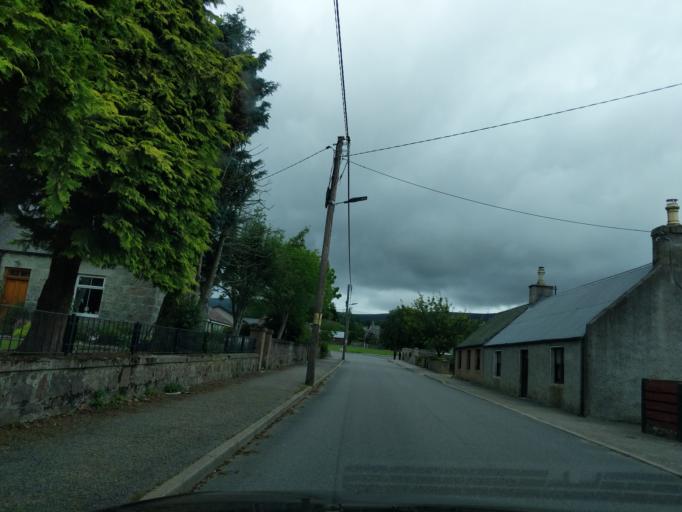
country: GB
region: Scotland
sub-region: Aberdeenshire
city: Aboyne
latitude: 57.1295
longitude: -2.8607
